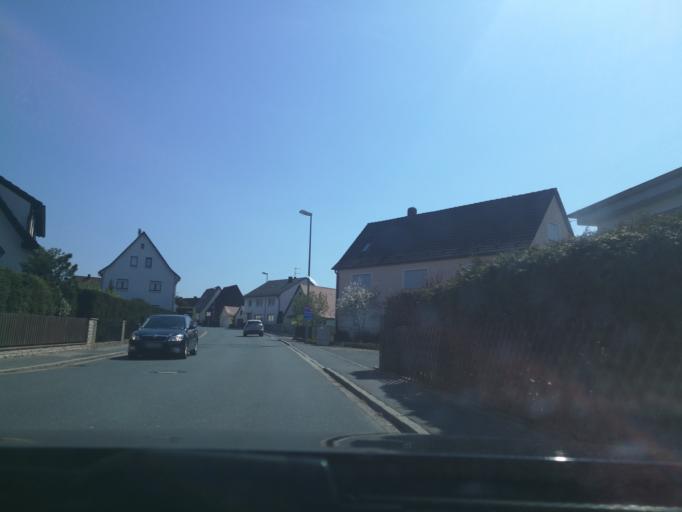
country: DE
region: Bavaria
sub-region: Regierungsbezirk Mittelfranken
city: Leinburg
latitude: 49.4614
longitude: 11.2851
